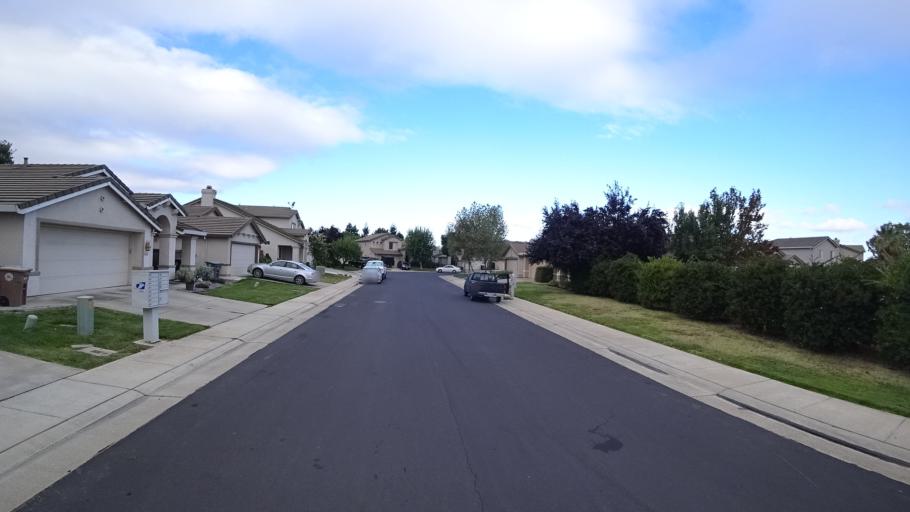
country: US
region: California
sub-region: Sacramento County
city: Laguna
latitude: 38.4318
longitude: -121.4198
